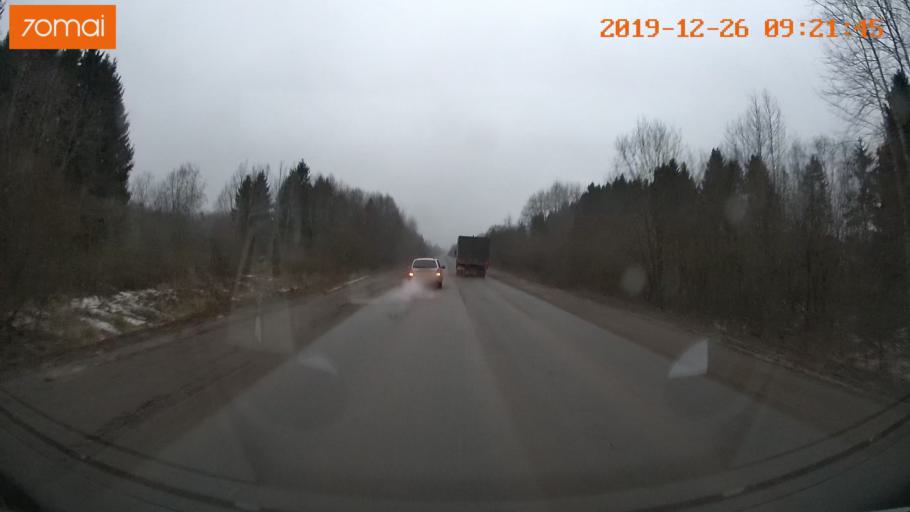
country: RU
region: Vologda
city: Gryazovets
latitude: 58.9722
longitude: 40.2228
